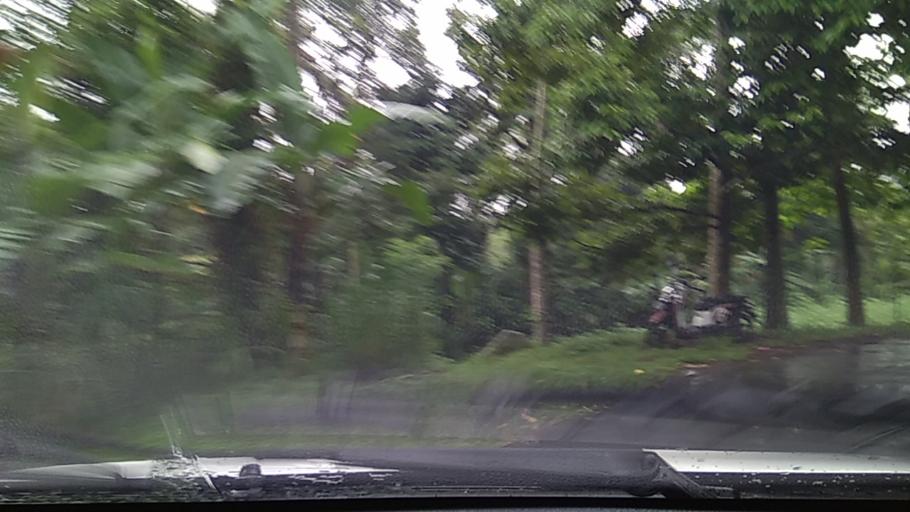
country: ID
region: Bali
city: Tiyingtali Kelod
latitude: -8.4056
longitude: 115.6269
